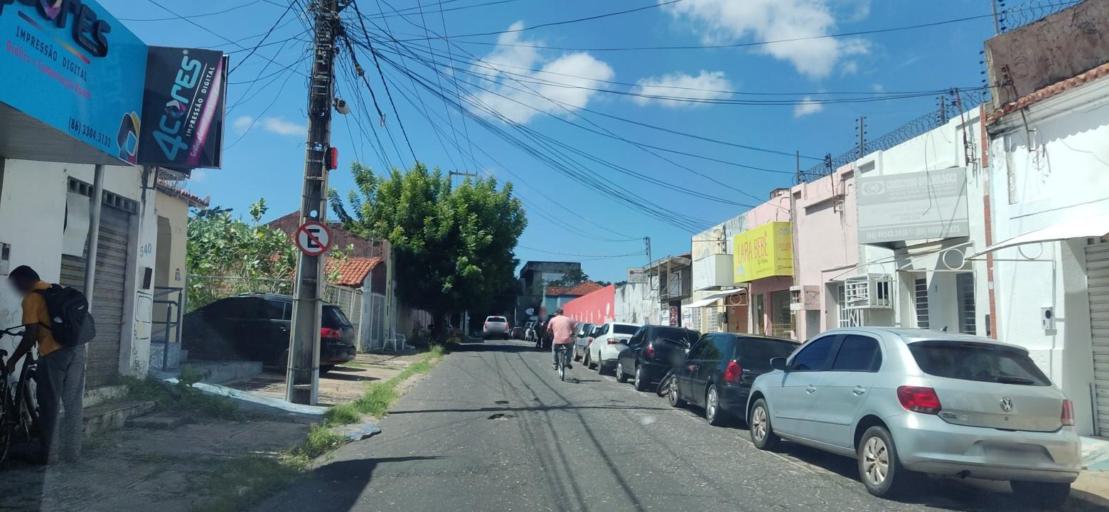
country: BR
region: Piaui
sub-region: Teresina
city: Teresina
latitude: -5.0864
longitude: -42.8144
